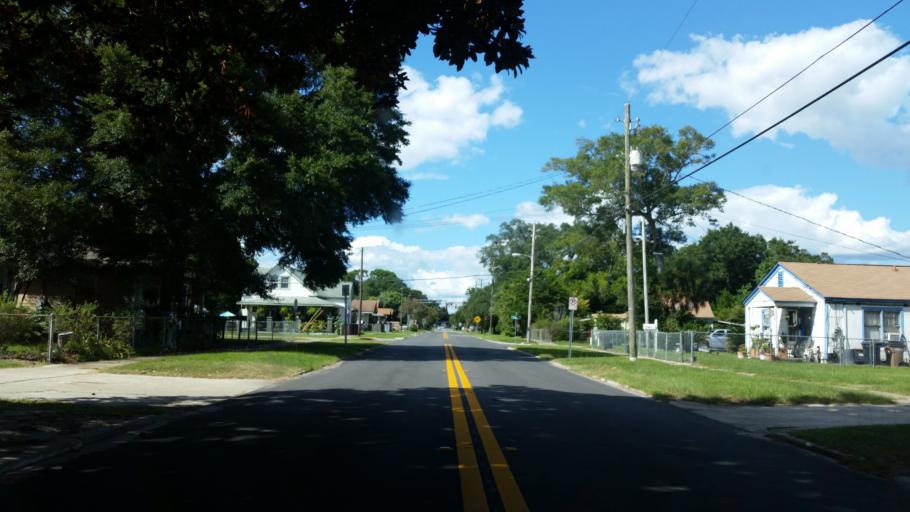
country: US
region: Florida
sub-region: Escambia County
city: Pensacola
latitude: 30.4039
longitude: -87.2310
